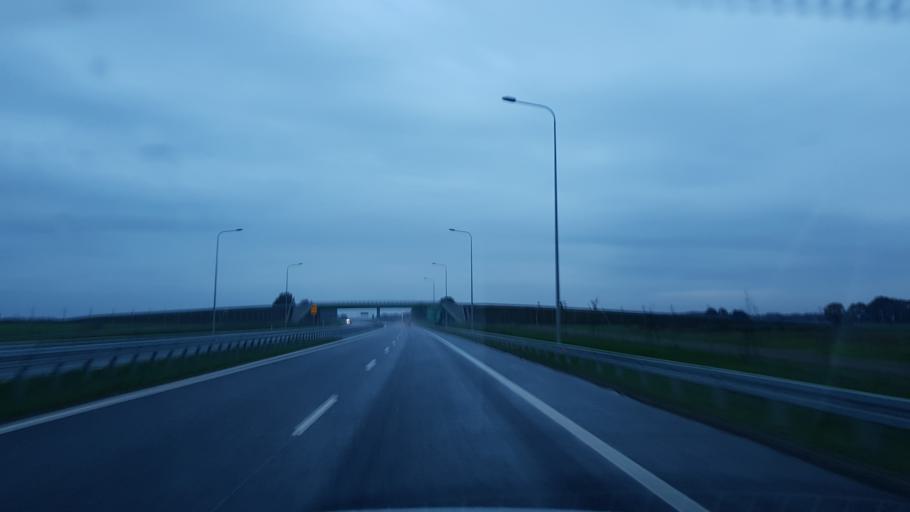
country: PL
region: West Pomeranian Voivodeship
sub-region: Powiat gryficki
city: Brojce
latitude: 53.8815
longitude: 15.3780
